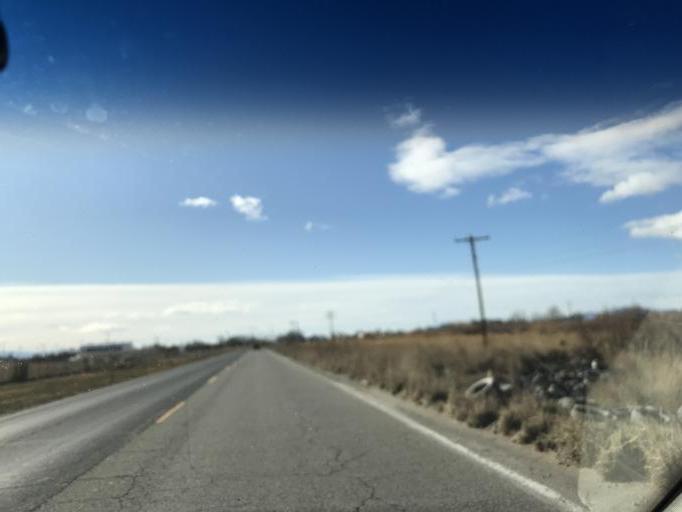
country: US
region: Utah
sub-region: Davis County
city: North Salt Lake
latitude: 40.8168
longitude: -111.9352
